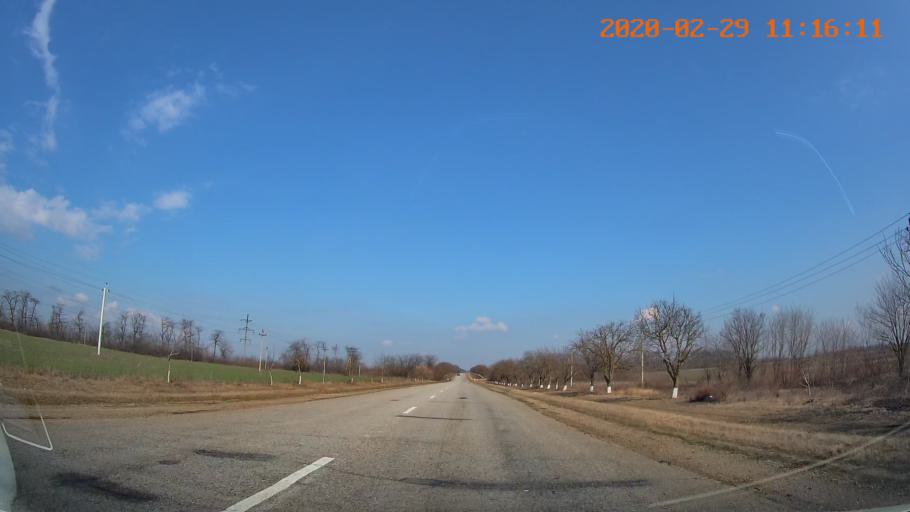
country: MD
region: Telenesti
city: Dubasari
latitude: 47.3051
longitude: 29.1671
